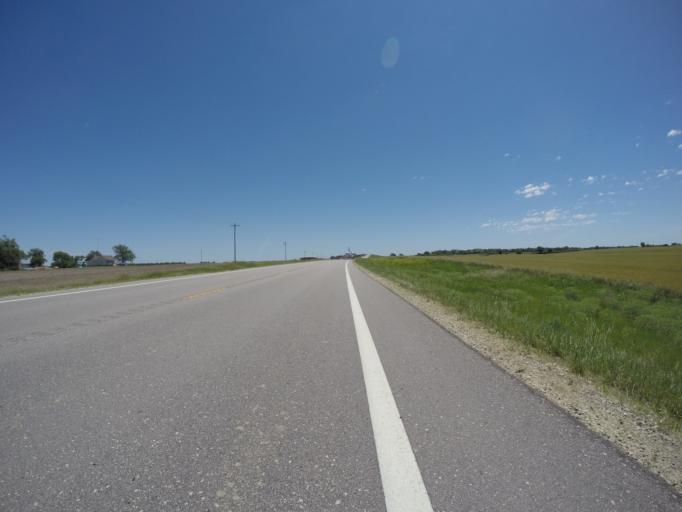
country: US
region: Kansas
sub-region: Republic County
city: Belleville
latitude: 39.8130
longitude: -97.7252
